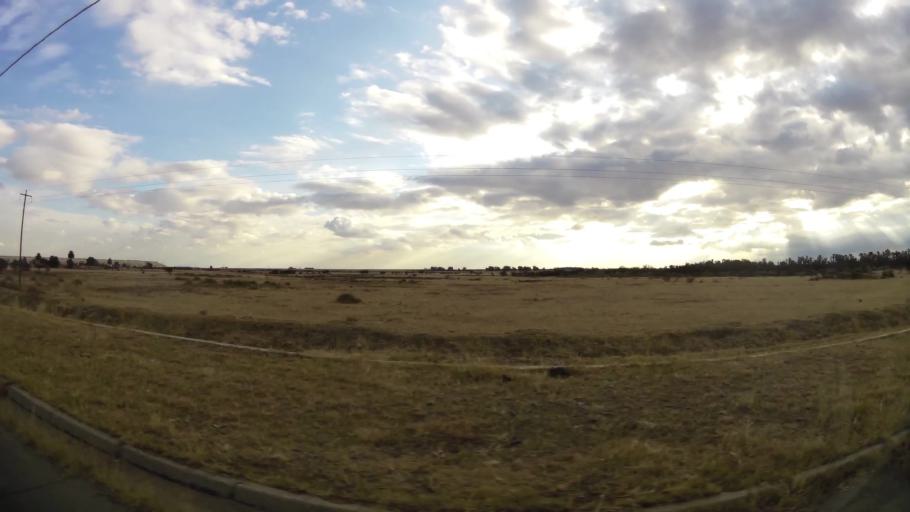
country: ZA
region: Orange Free State
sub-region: Lejweleputswa District Municipality
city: Welkom
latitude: -28.0076
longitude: 26.7100
